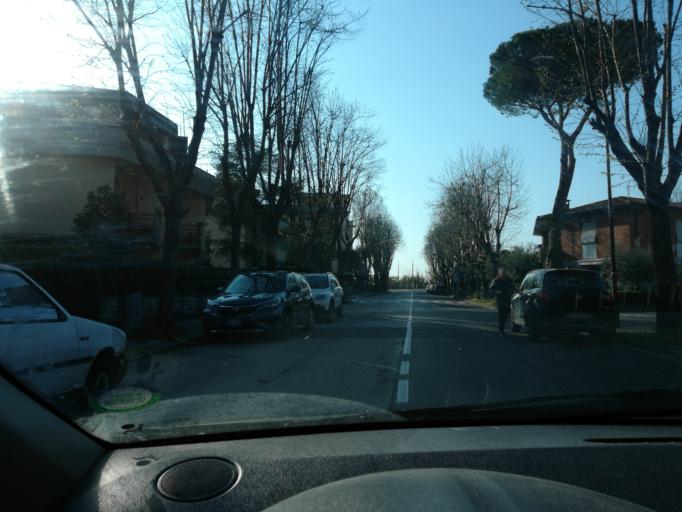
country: IT
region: Tuscany
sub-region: Province of Pisa
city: Pisa
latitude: 43.7332
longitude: 10.4022
